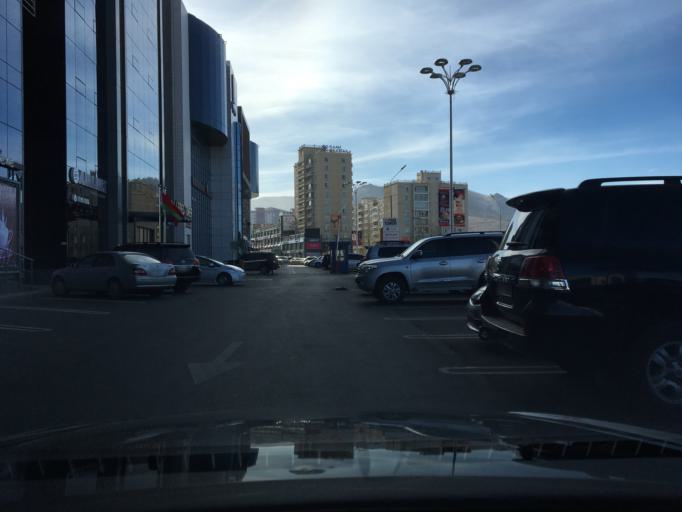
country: MN
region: Ulaanbaatar
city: Ulaanbaatar
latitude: 47.8979
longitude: 106.9089
